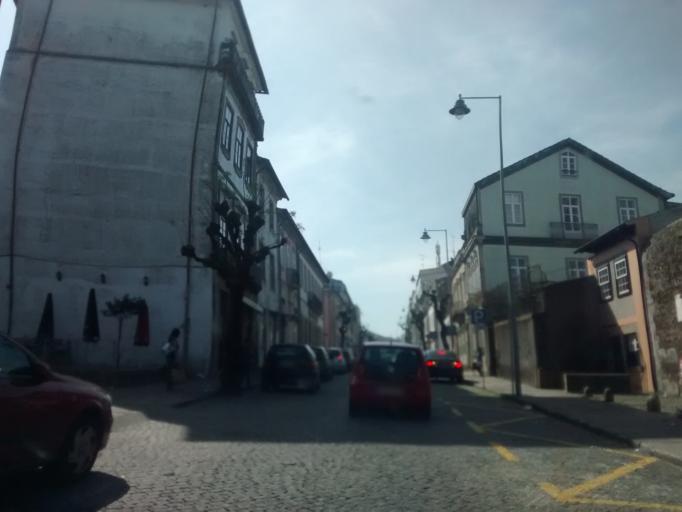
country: PT
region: Braga
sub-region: Braga
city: Braga
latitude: 41.5494
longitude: -8.4285
